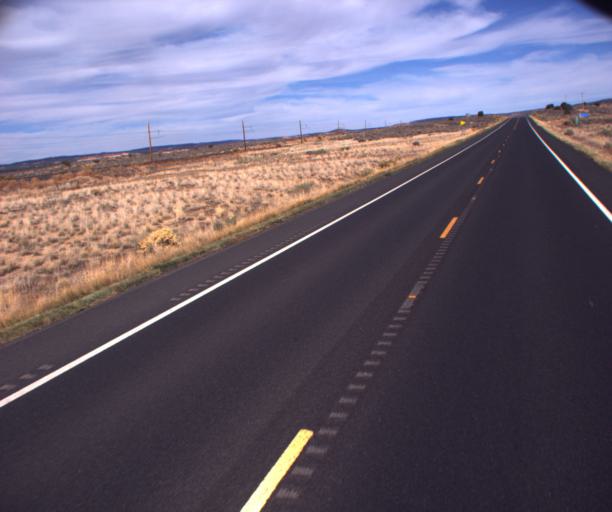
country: US
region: Arizona
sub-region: Navajo County
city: Kayenta
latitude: 36.5371
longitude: -110.5554
